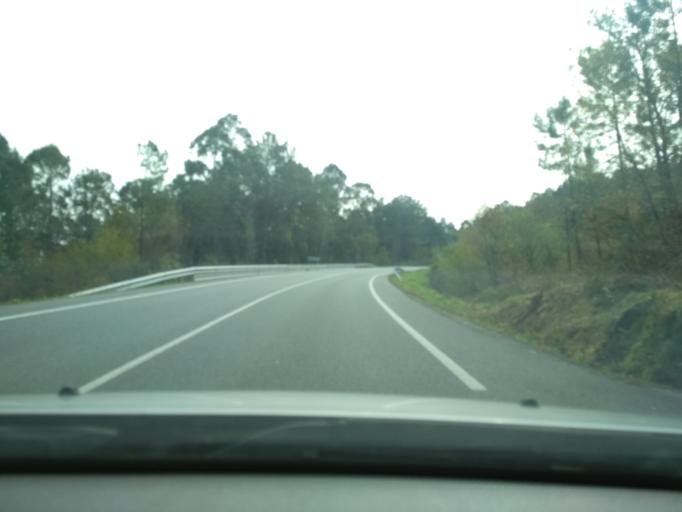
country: ES
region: Galicia
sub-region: Provincia de Pontevedra
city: Catoira
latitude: 42.6531
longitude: -8.6975
